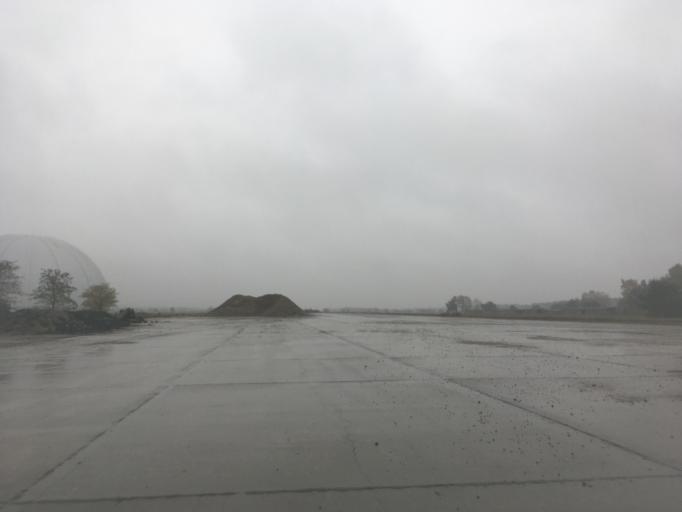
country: DE
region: Brandenburg
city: Halbe
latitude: 52.0366
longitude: 13.7348
